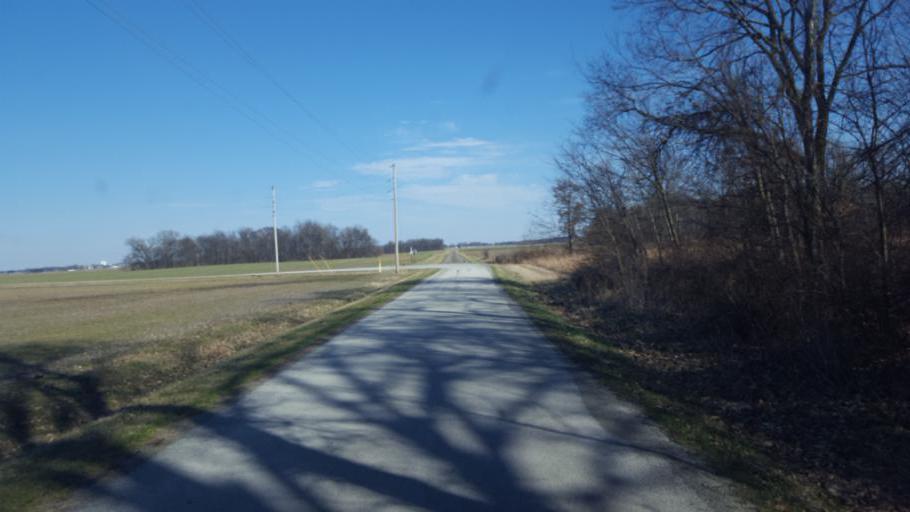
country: US
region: Ohio
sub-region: Marion County
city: Marion
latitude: 40.7021
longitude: -83.2085
